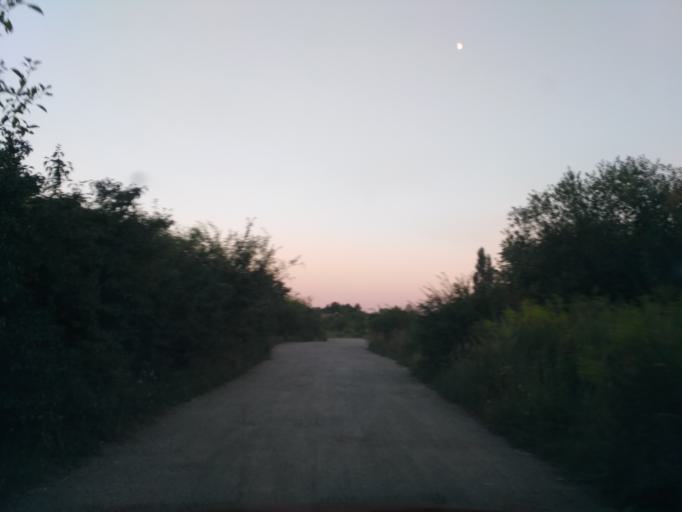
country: SK
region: Kosicky
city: Kosice
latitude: 48.7230
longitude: 21.2210
